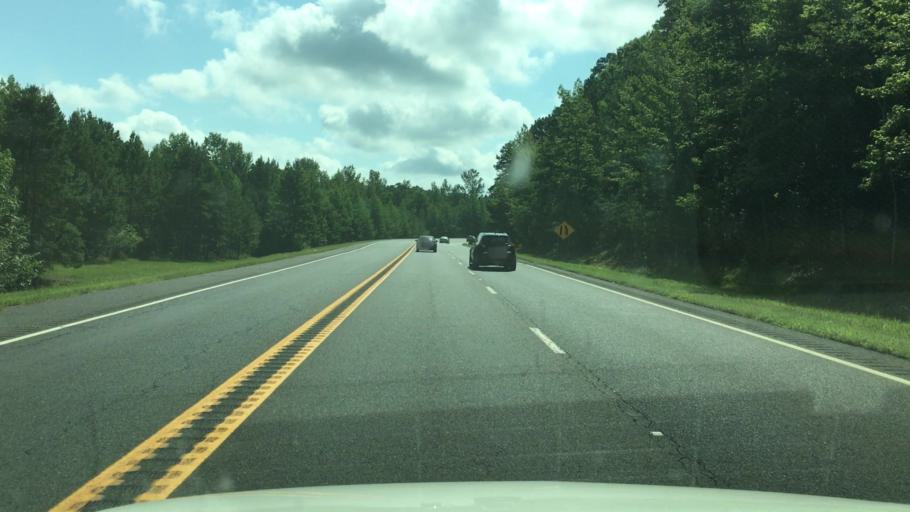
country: US
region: Arkansas
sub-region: Garland County
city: Lake Hamilton
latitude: 34.3686
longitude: -93.1662
